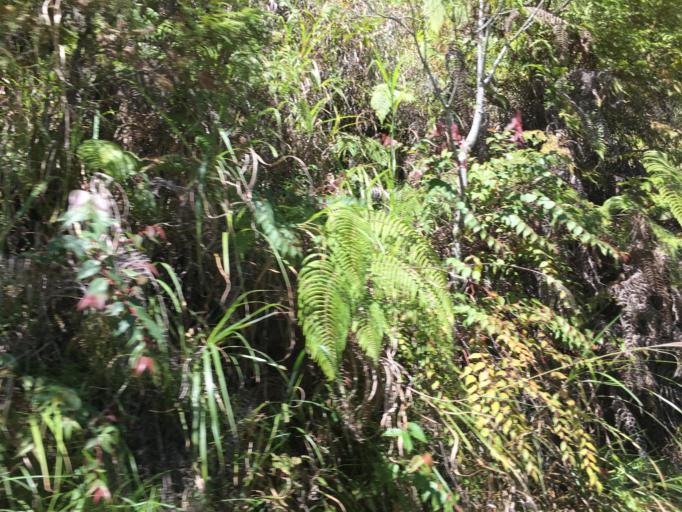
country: TW
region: Taiwan
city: Daxi
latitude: 24.5374
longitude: 121.4018
